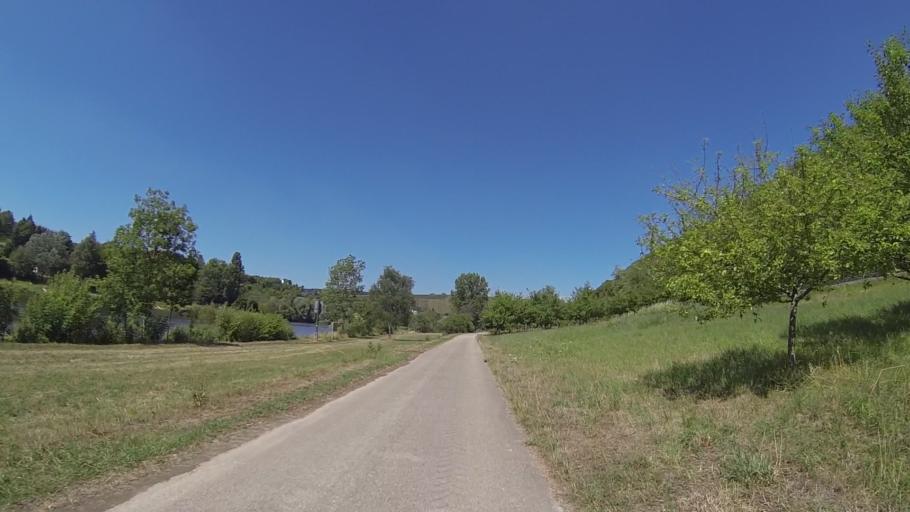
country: LU
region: Grevenmacher
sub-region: Canton de Remich
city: Lenningen
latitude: 49.5840
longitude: 6.3794
